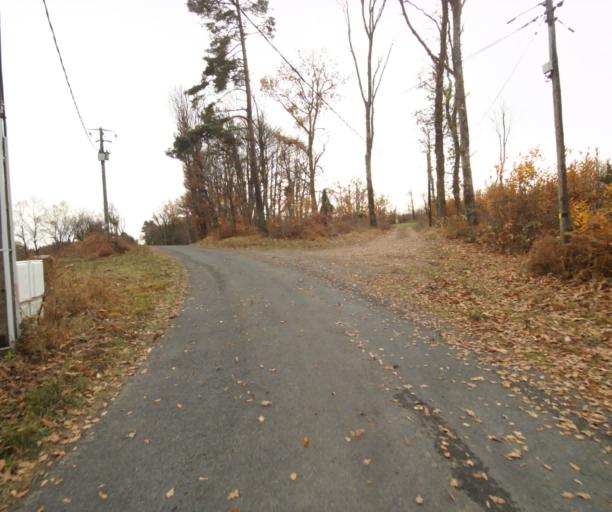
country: FR
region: Limousin
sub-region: Departement de la Correze
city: Sainte-Fortunade
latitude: 45.1911
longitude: 1.7532
